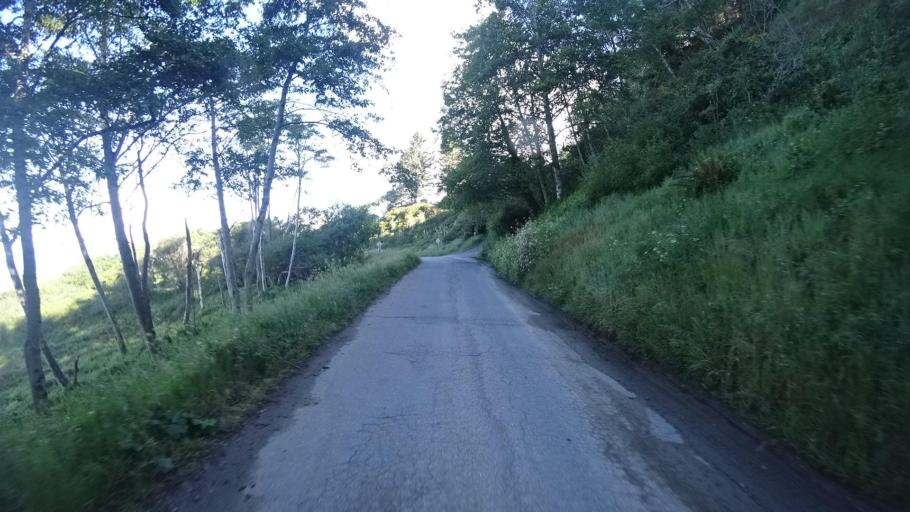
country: US
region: California
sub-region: Humboldt County
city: Westhaven-Moonstone
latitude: 41.0391
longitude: -124.1184
